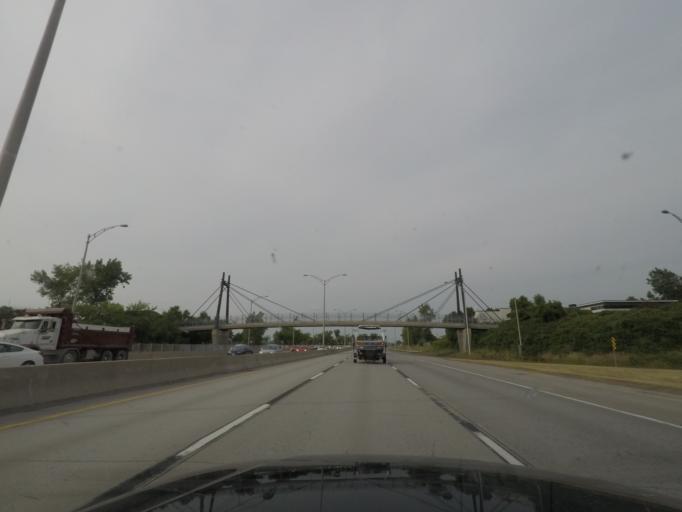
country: CA
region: Quebec
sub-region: Monteregie
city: La Prairie
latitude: 45.4177
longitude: -73.4994
